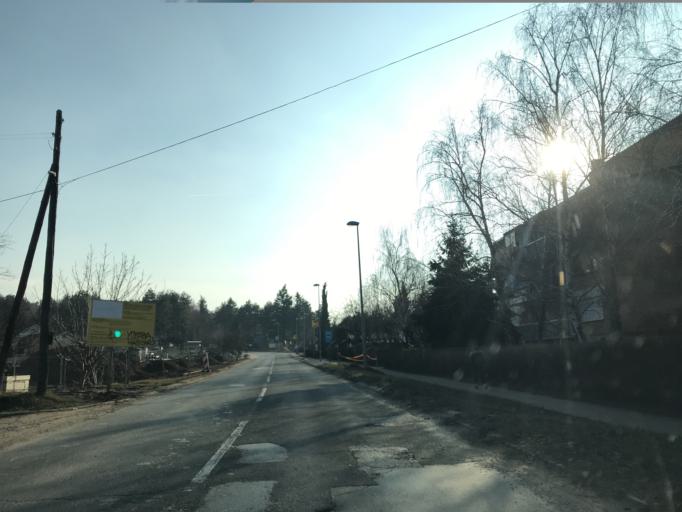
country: RS
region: Autonomna Pokrajina Vojvodina
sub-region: Juznobacki Okrug
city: Petrovaradin
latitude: 45.2245
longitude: 19.8559
